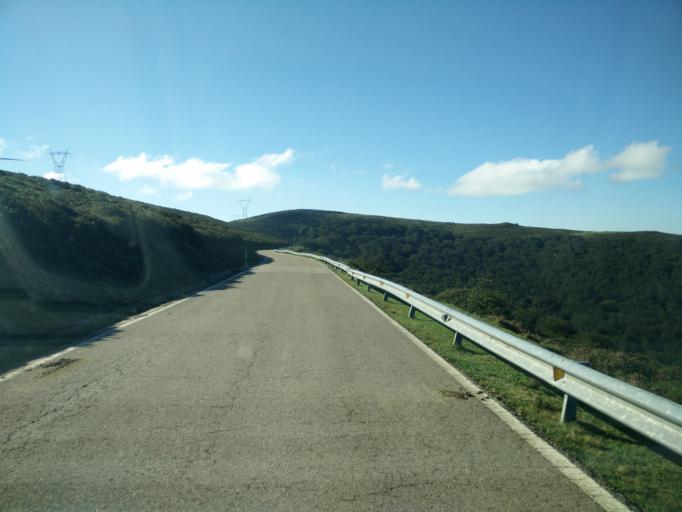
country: ES
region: Cantabria
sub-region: Provincia de Cantabria
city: San Pedro del Romeral
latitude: 43.0474
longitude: -3.8514
